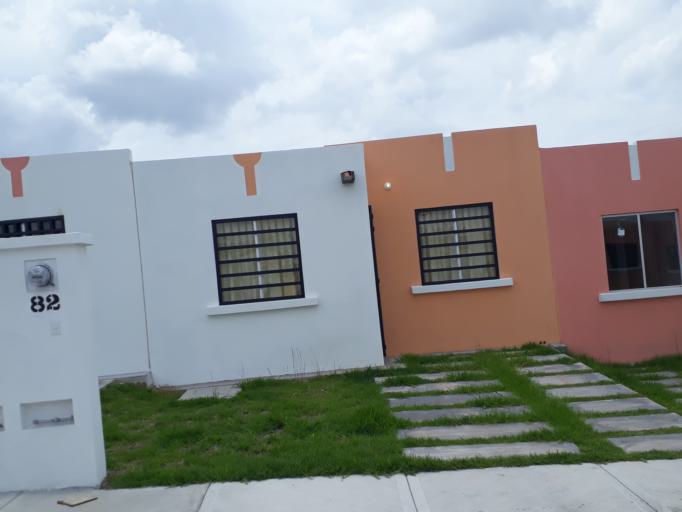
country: MX
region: Aguascalientes
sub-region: Aguascalientes
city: San Sebastian [Fraccionamiento]
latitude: 21.8069
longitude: -102.2660
